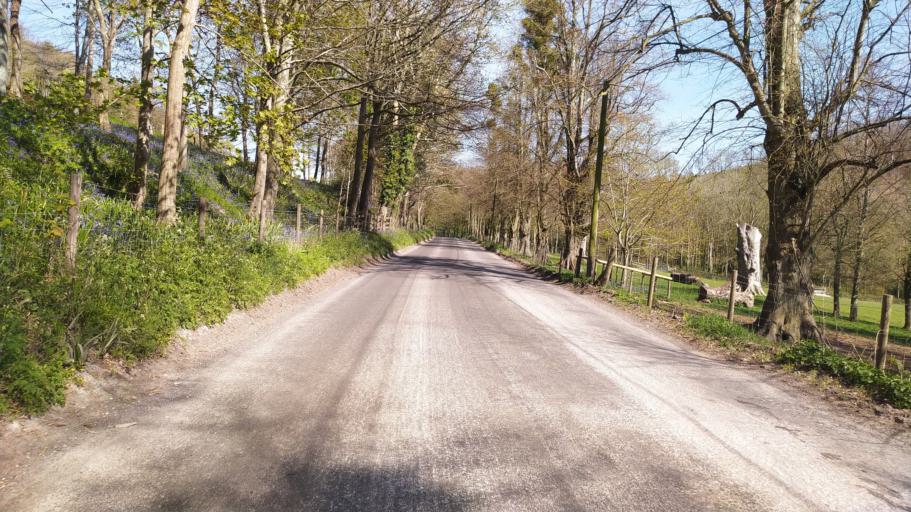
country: GB
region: England
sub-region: Dorset
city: Blandford Forum
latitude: 50.9008
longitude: -2.2136
